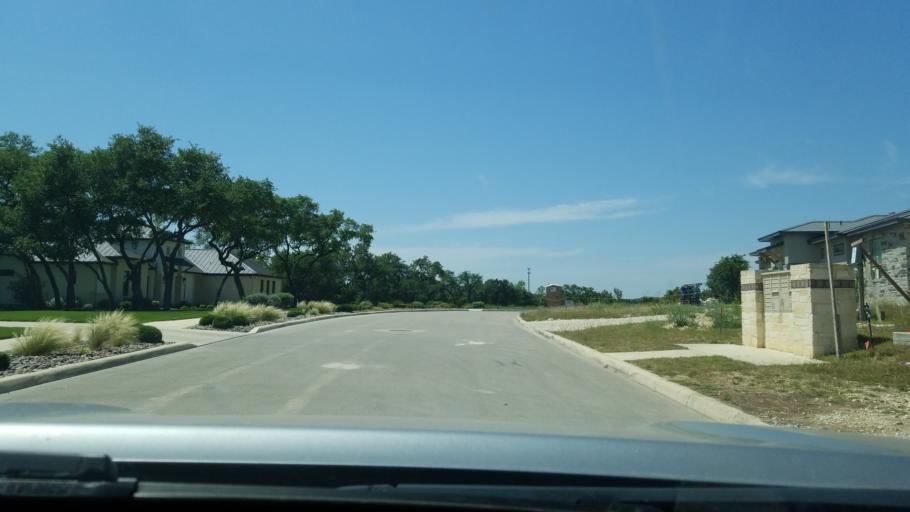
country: US
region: Texas
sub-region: Kendall County
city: Boerne
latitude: 29.7928
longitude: -98.6925
